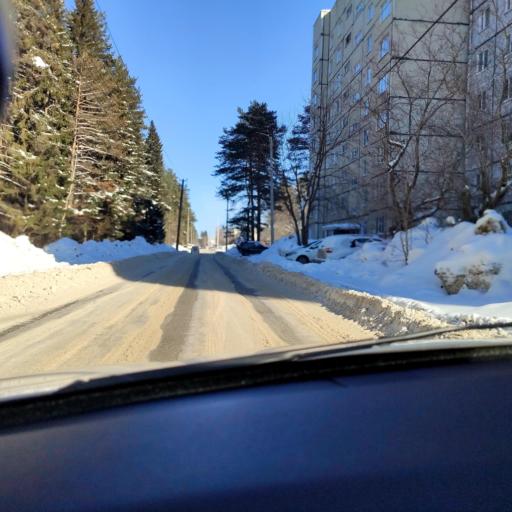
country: RU
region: Perm
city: Dobryanka
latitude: 58.4711
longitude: 56.3951
